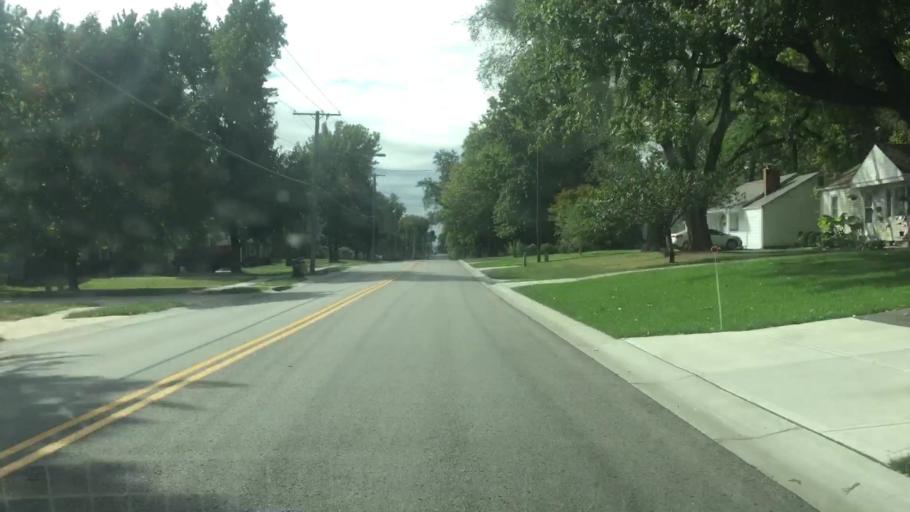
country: US
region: Kansas
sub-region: Johnson County
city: Shawnee
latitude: 39.0359
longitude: -94.7239
